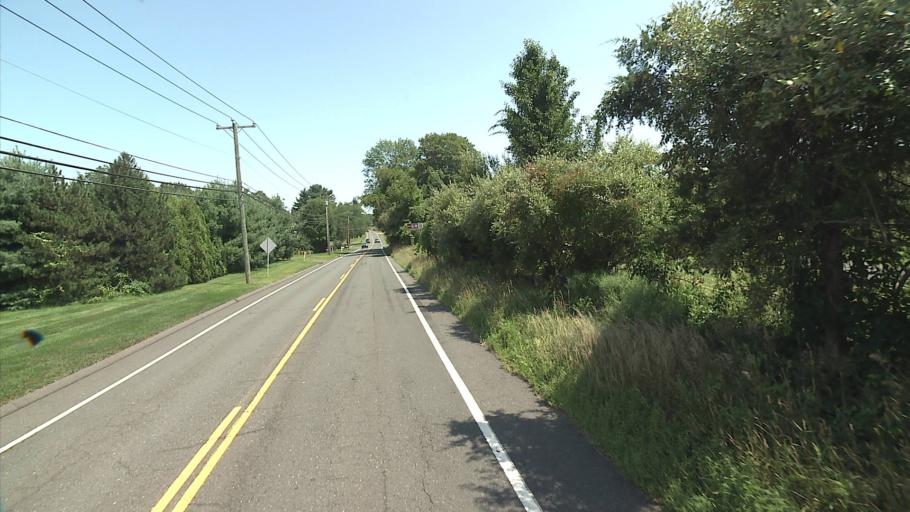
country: US
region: Connecticut
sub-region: Hartford County
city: Salmon Brook
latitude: 41.9536
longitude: -72.8139
